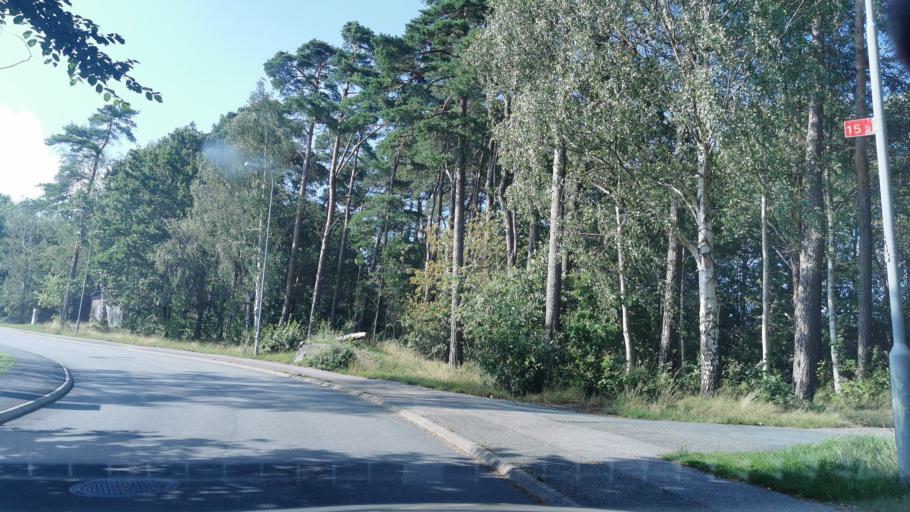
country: SE
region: Vaestra Goetaland
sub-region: Goteborg
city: Majorna
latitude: 57.6443
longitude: 11.9105
